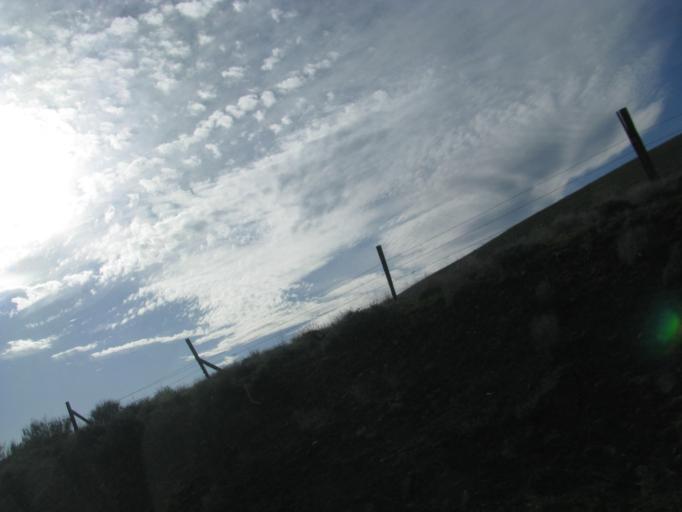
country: US
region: Washington
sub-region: Spokane County
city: Medical Lake
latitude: 47.3549
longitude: -117.8524
